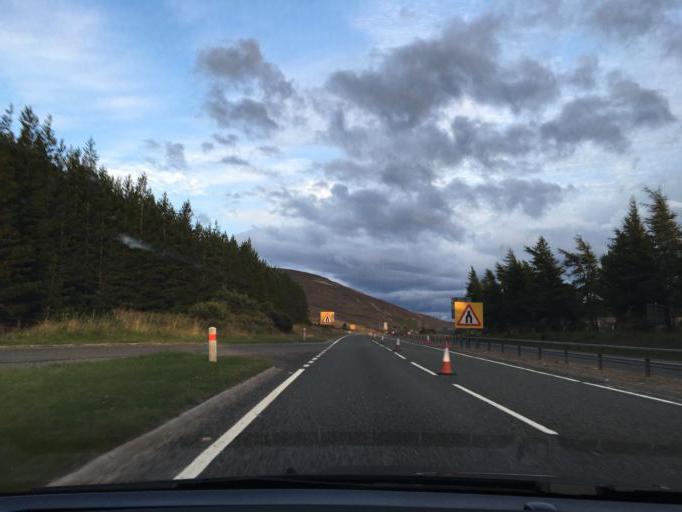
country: GB
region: Scotland
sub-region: Highland
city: Aviemore
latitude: 57.3111
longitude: -3.9461
